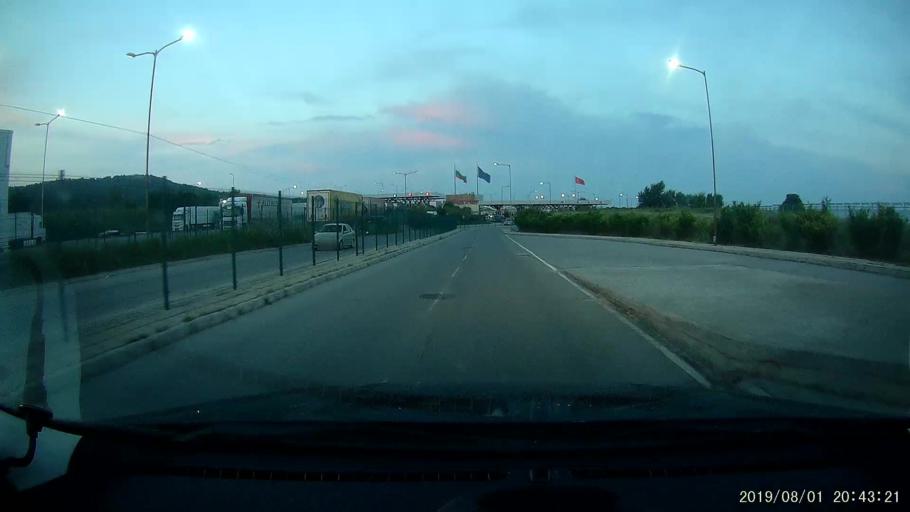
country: TR
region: Edirne
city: Lalapasa
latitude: 41.9625
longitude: 26.6028
